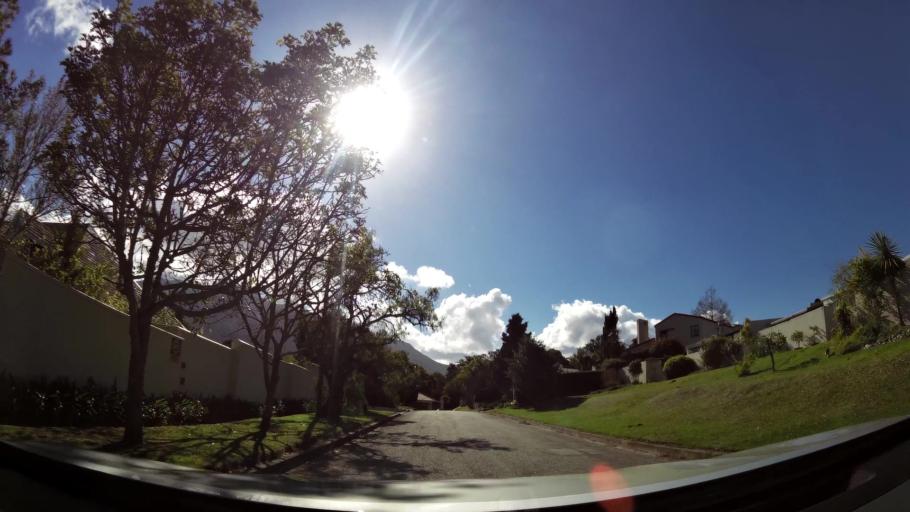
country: ZA
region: Western Cape
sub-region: Eden District Municipality
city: George
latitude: -33.9518
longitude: 22.4586
